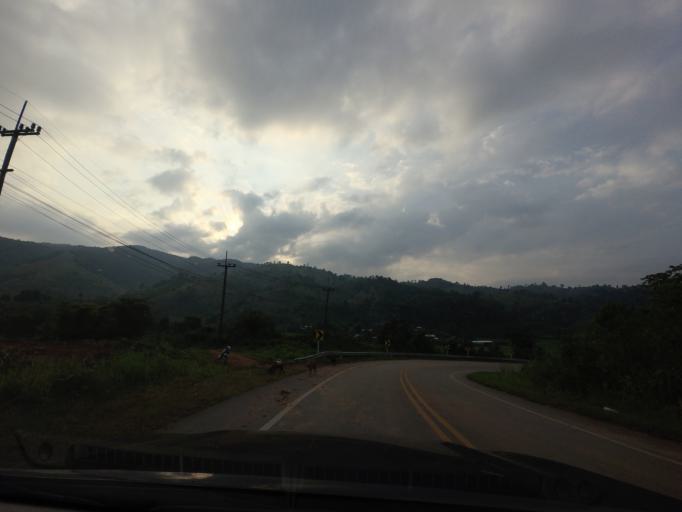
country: TH
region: Loei
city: Na Haeo
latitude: 17.3783
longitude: 101.0438
